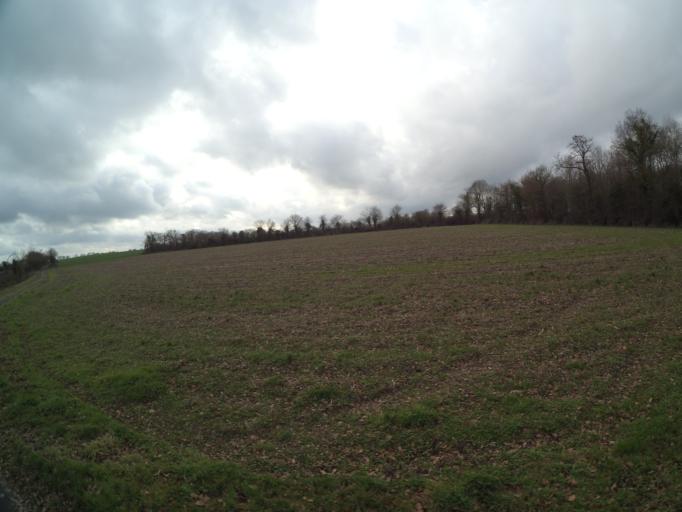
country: FR
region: Pays de la Loire
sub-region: Departement de la Vendee
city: La Bernardiere
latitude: 47.0278
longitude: -1.2924
